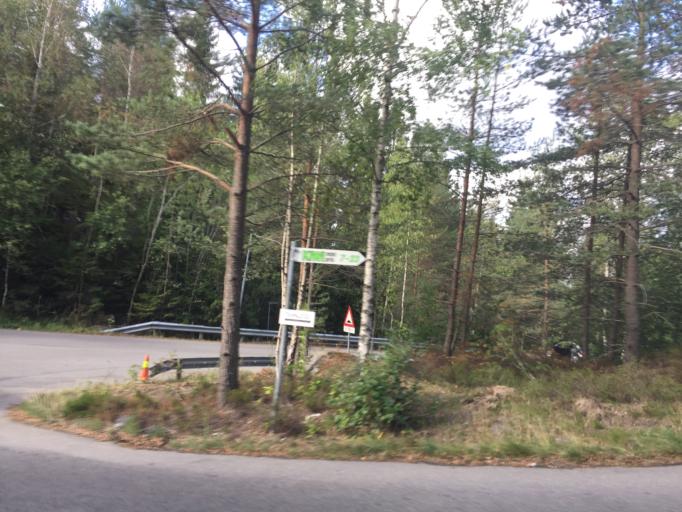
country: NO
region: Akershus
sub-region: Skedsmo
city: Lillestrom
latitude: 59.9302
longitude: 11.0343
